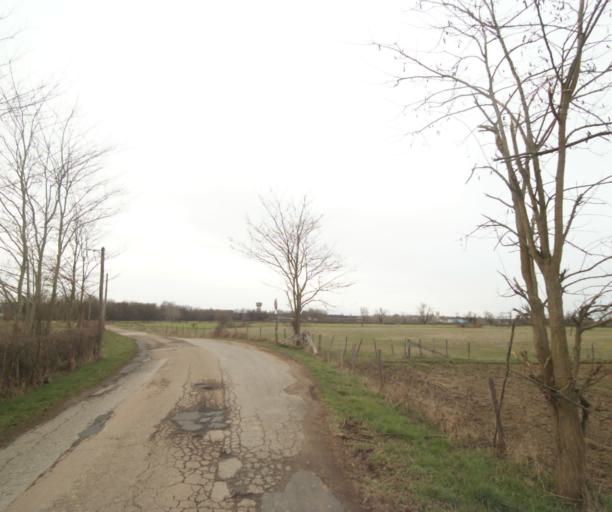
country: FR
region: Rhone-Alpes
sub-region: Departement de la Loire
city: Perreux
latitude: 46.0649
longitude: 4.1027
